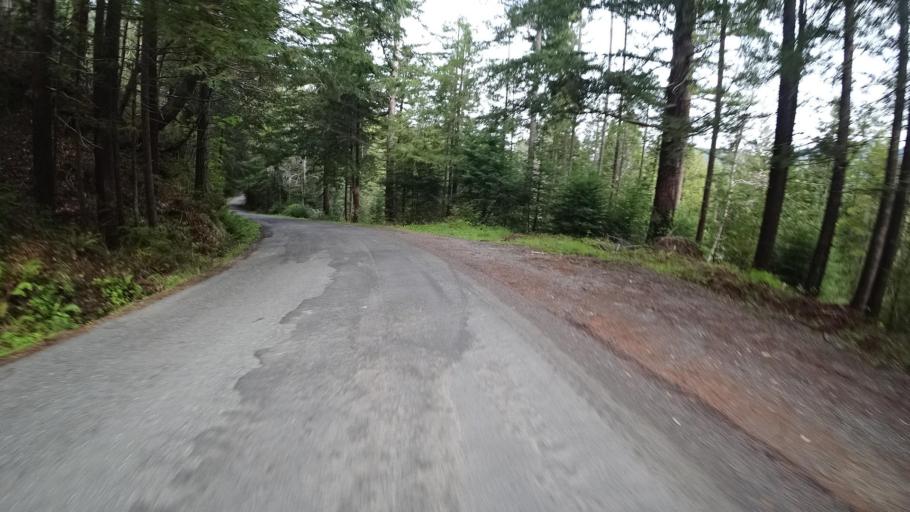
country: US
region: California
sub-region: Humboldt County
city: Redway
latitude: 40.3366
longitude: -123.8542
